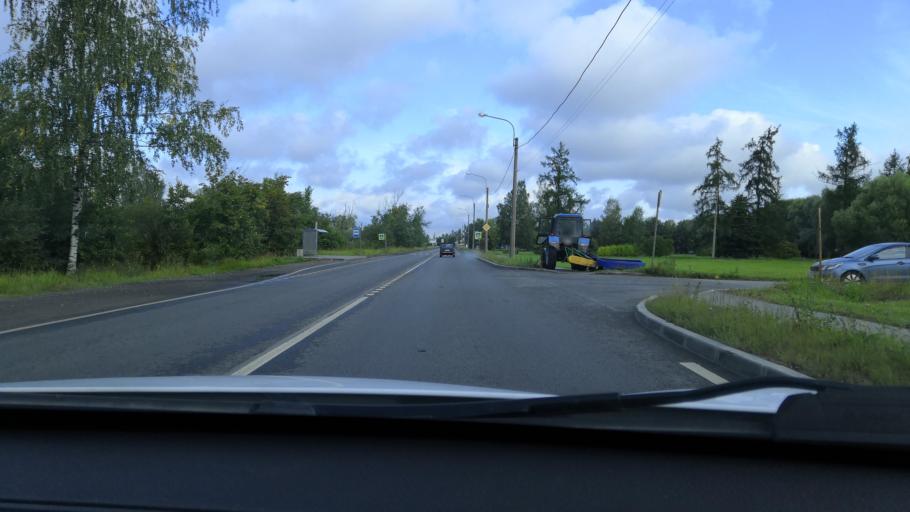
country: RU
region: St.-Petersburg
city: Tyarlevo
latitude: 59.7077
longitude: 30.4377
